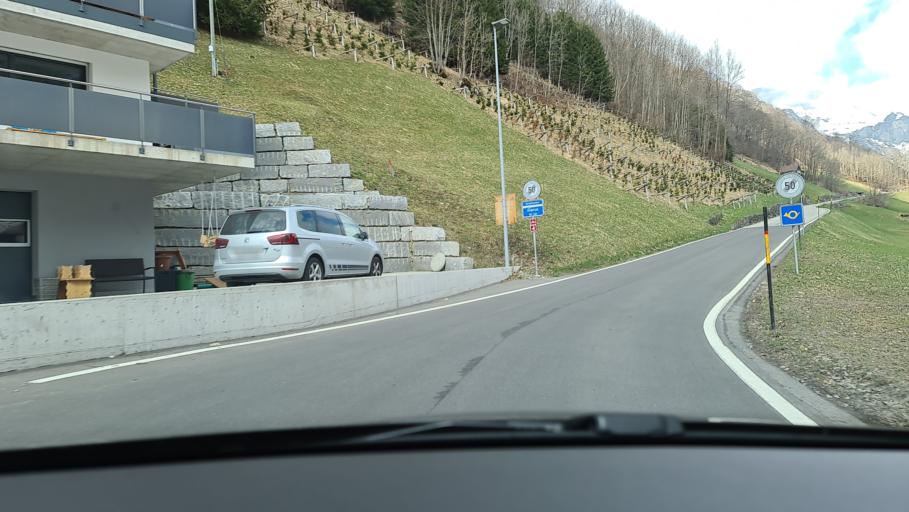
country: CH
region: Uri
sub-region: Uri
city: Burglen
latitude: 46.8644
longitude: 8.7723
